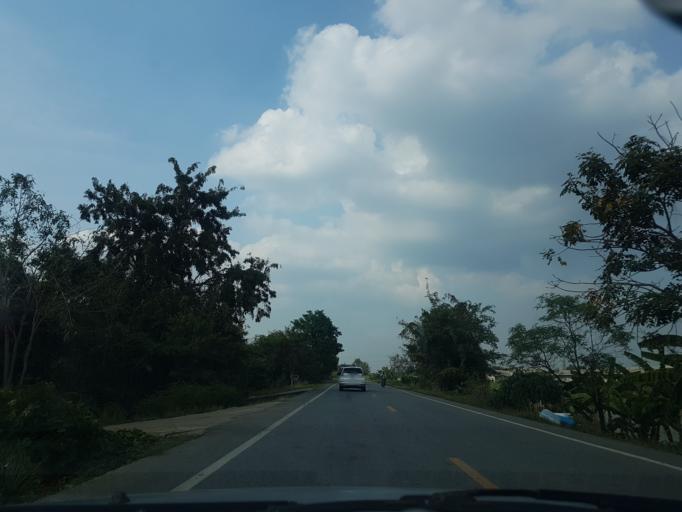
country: TH
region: Phra Nakhon Si Ayutthaya
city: Phachi
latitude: 14.4301
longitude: 100.7748
